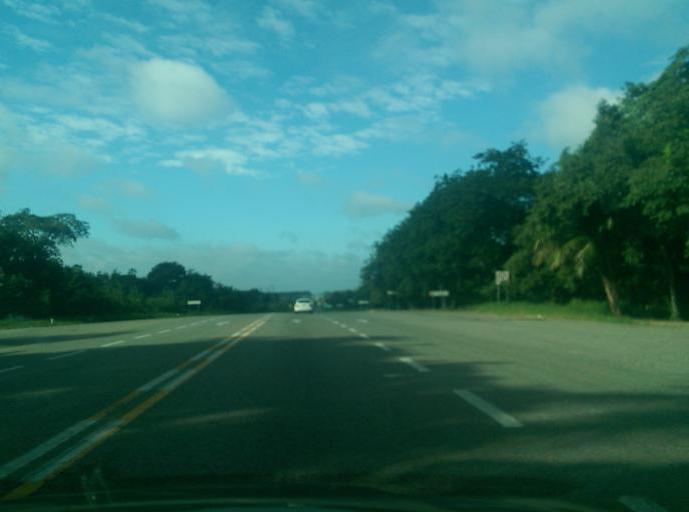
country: MX
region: Chiapas
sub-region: Catazaja
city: Catazaja
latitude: 17.7113
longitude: -92.0139
